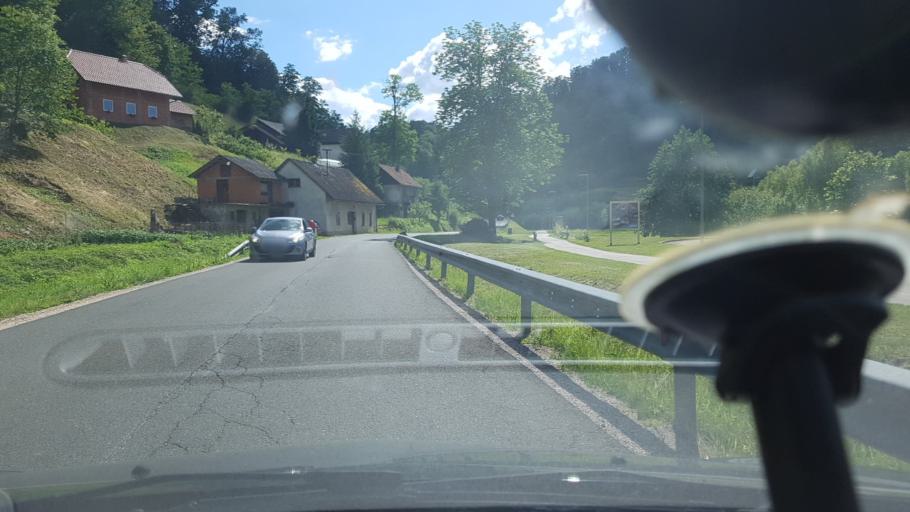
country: SI
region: Rogatec
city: Rogatec
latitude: 46.2330
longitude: 15.7022
